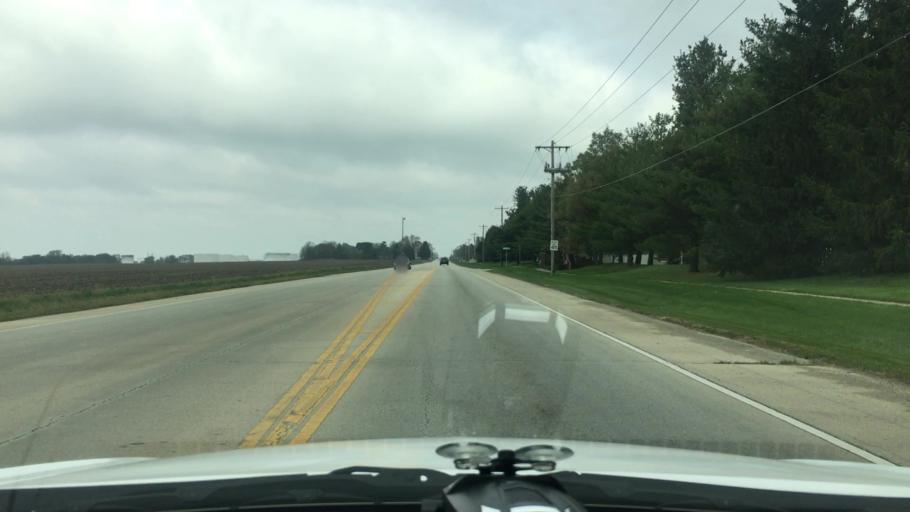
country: US
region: Illinois
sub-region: Champaign County
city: Champaign
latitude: 40.0996
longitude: -88.3143
